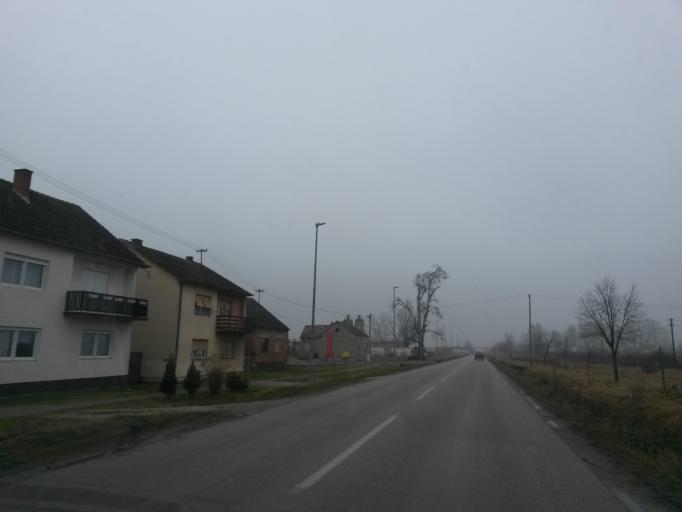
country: HR
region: Vukovarsko-Srijemska
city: Zupanja
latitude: 45.0984
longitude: 18.6981
